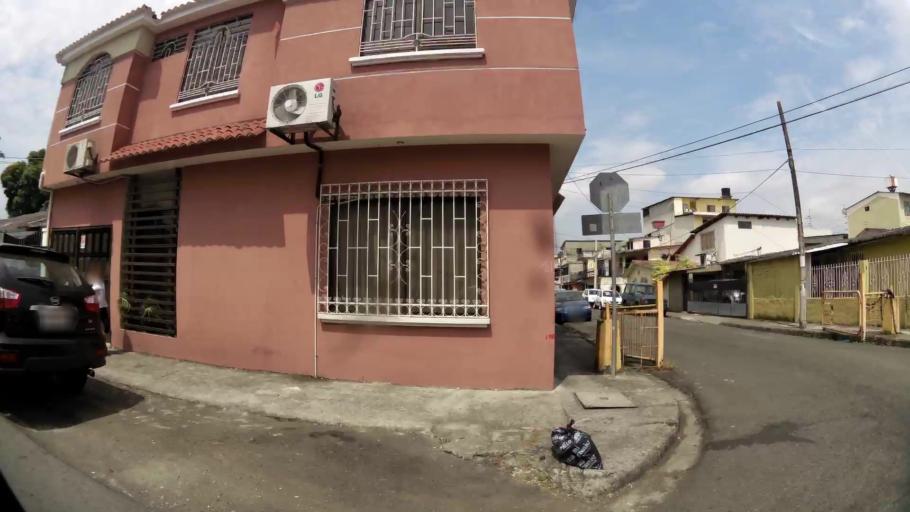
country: EC
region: Guayas
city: Eloy Alfaro
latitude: -2.1440
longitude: -79.9008
